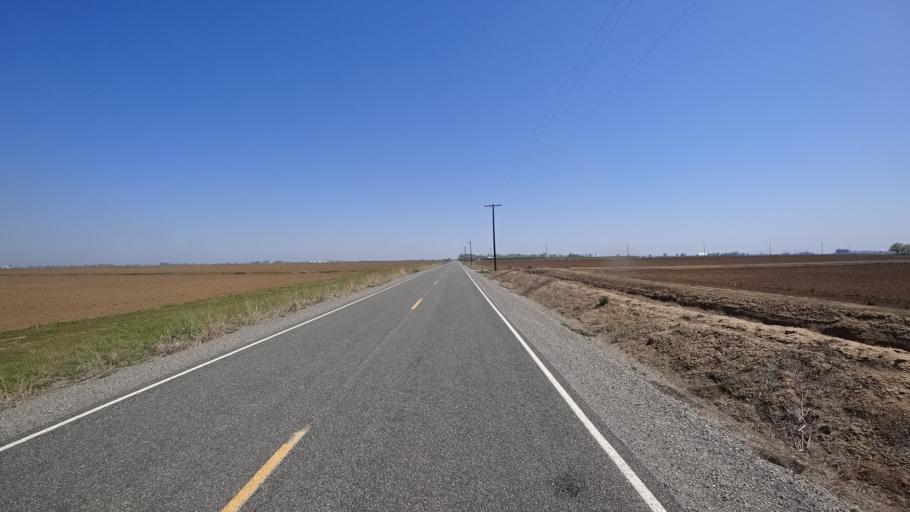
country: US
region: California
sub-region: Glenn County
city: Willows
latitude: 39.4946
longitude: -122.1596
